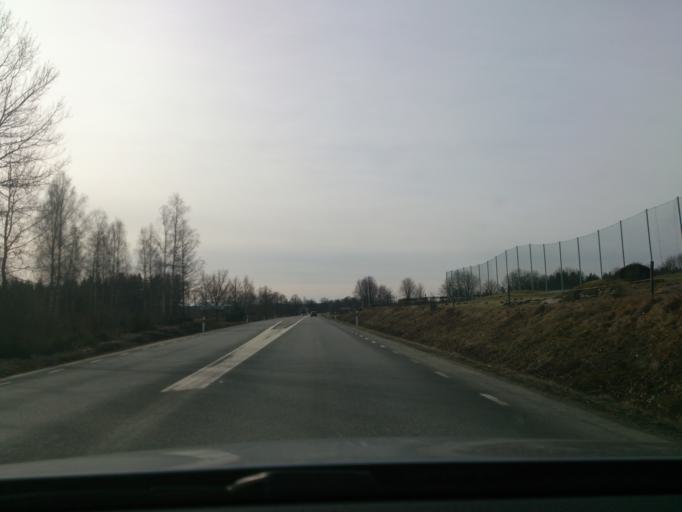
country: SE
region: Kronoberg
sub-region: Alvesta Kommun
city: Moheda
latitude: 56.9661
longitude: 14.5714
